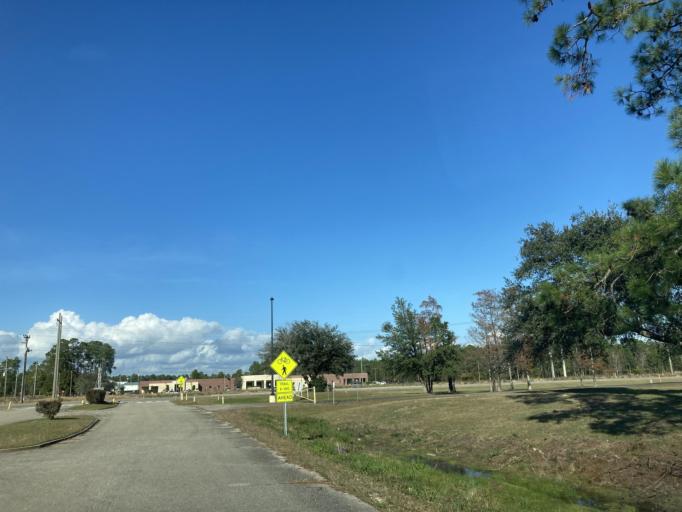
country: US
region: Mississippi
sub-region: Harrison County
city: West Gulfport
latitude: 30.4334
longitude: -89.0563
